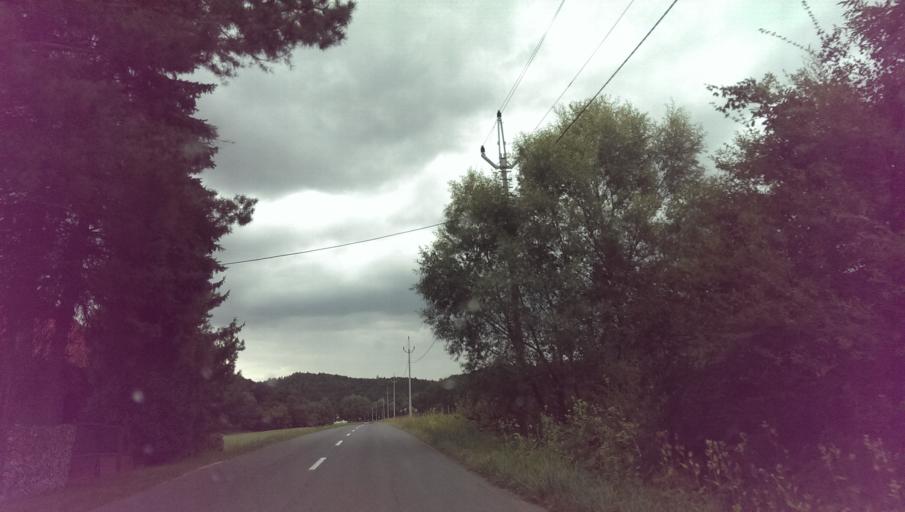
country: CZ
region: South Moravian
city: Velka nad Velickou
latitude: 48.8894
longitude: 17.5768
